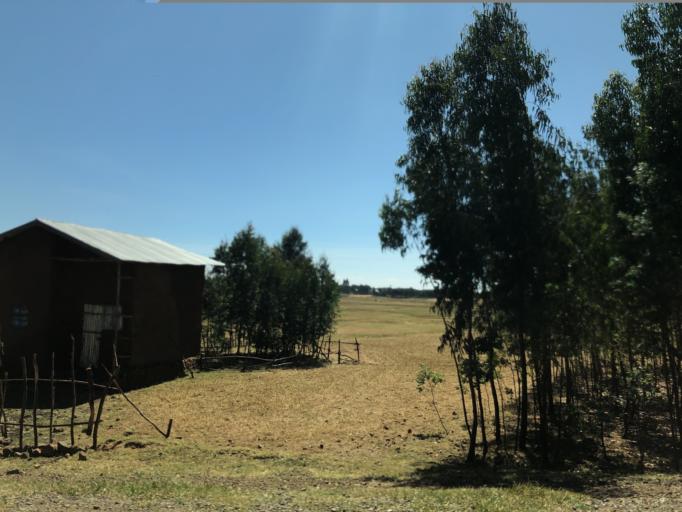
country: ET
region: Amhara
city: Lalibela
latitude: 11.6785
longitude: 38.8976
